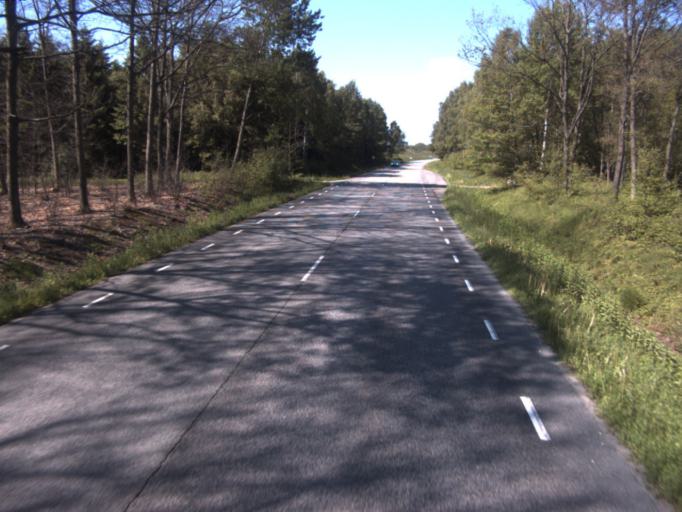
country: SE
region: Skane
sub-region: Helsingborg
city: Odakra
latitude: 56.0533
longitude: 12.7728
